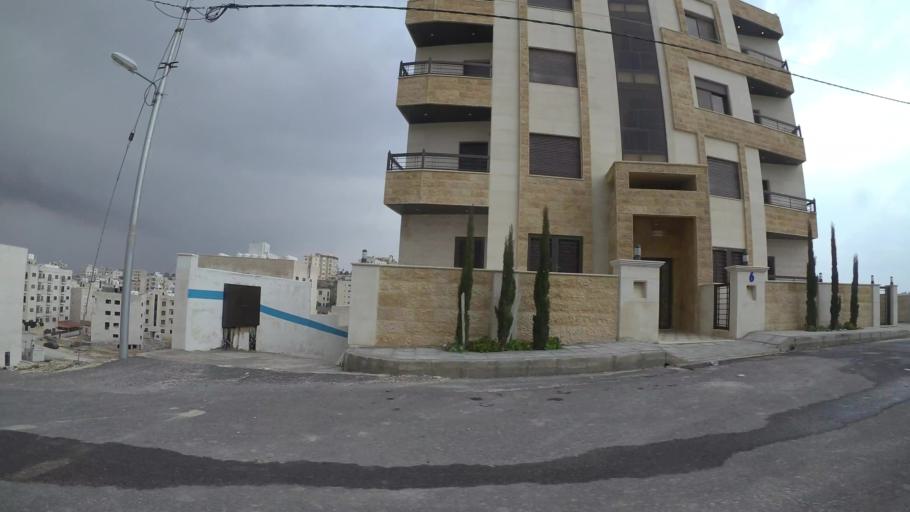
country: JO
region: Amman
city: Umm as Summaq
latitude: 31.8836
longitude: 35.8548
